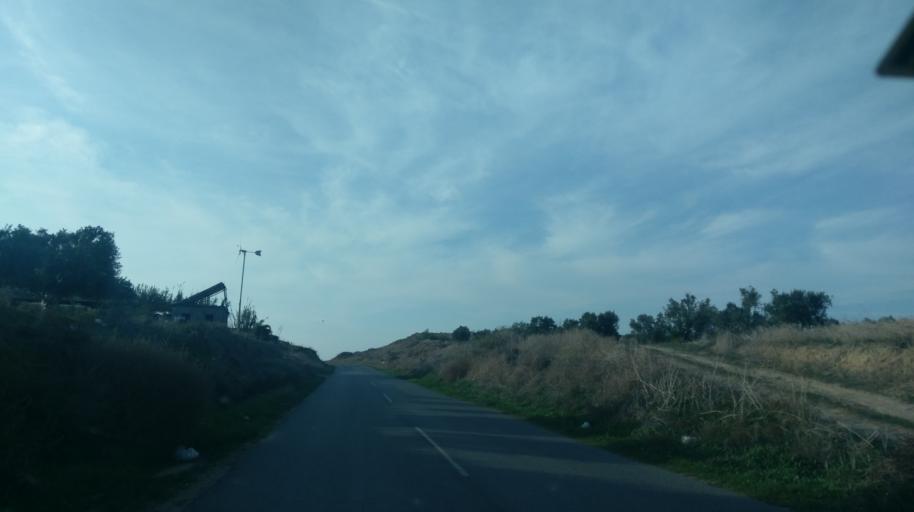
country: CY
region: Ammochostos
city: Achna
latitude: 35.1016
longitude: 33.7816
